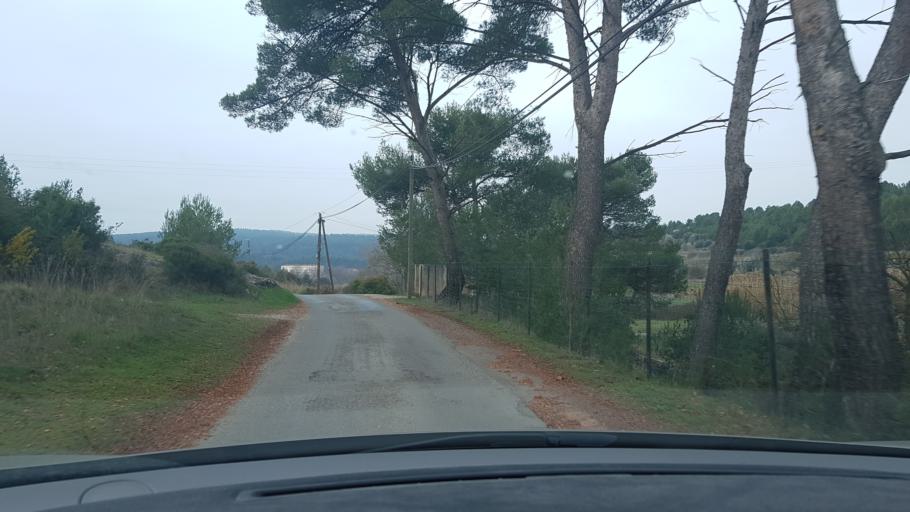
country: FR
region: Provence-Alpes-Cote d'Azur
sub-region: Departement des Bouches-du-Rhone
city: Gardanne
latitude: 43.4753
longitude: 5.4634
